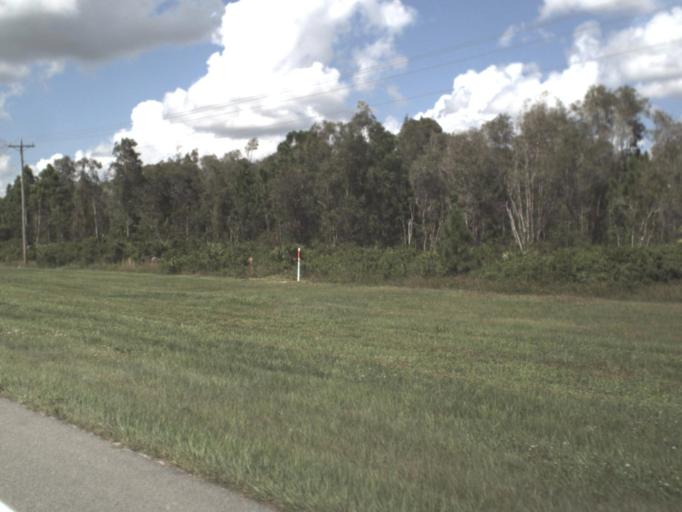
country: US
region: Florida
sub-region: Lee County
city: Lehigh Acres
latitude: 26.5321
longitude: -81.6175
